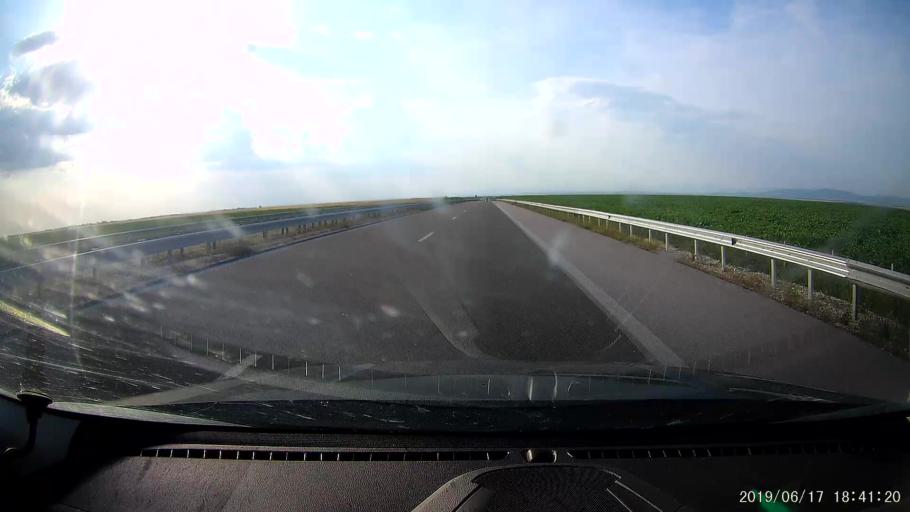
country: BG
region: Stara Zagora
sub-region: Obshtina Chirpan
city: Chirpan
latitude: 42.1705
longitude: 25.2574
